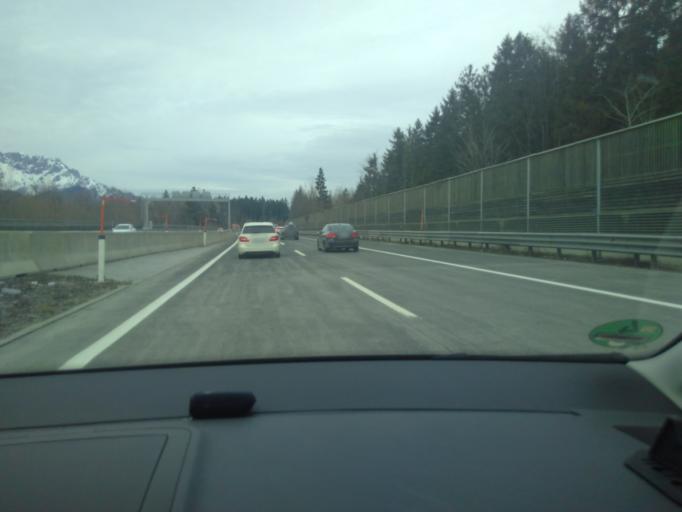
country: AT
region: Salzburg
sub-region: Politischer Bezirk Hallein
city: Adnet
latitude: 47.6567
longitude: 13.1340
